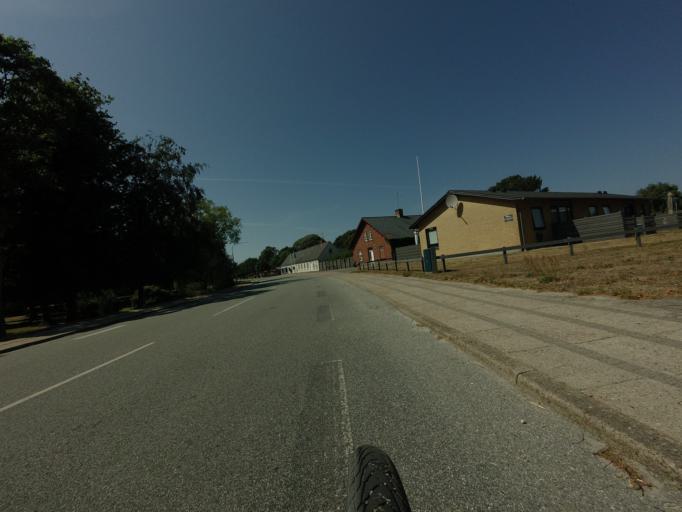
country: DK
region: North Denmark
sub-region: Laeso Kommune
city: Byrum
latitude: 57.2556
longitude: 11.0004
